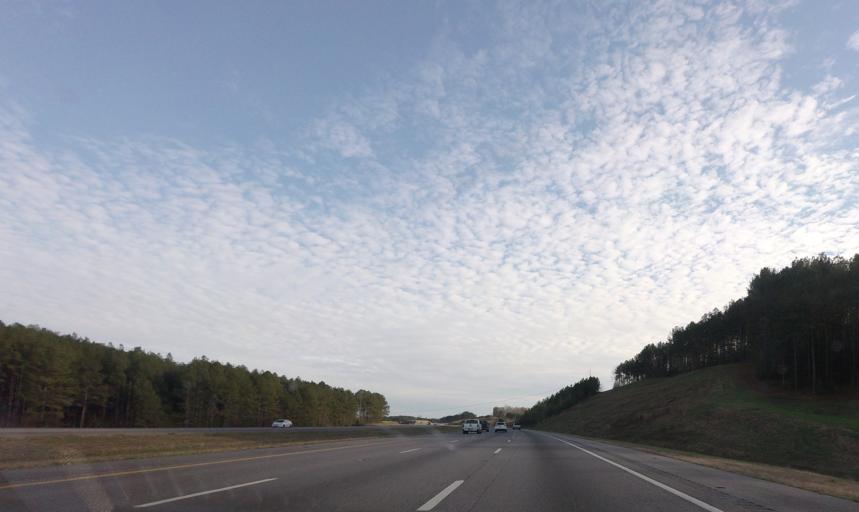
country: US
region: Alabama
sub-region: Walker County
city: Cordova
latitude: 33.7248
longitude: -87.1892
